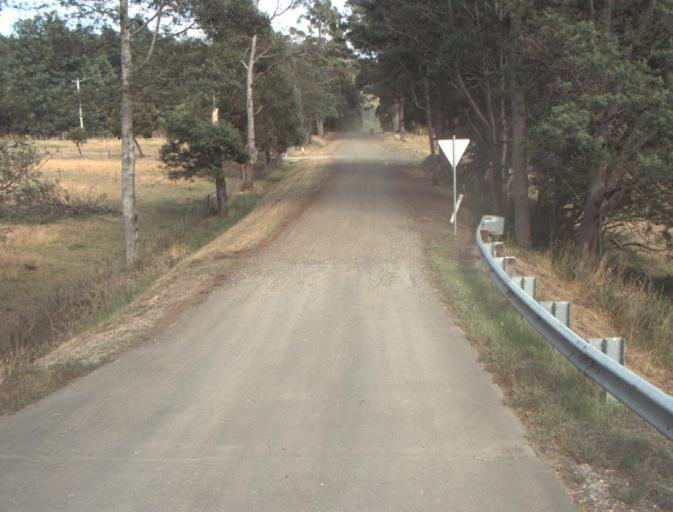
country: AU
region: Tasmania
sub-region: Launceston
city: Mayfield
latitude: -41.2921
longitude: 147.2155
